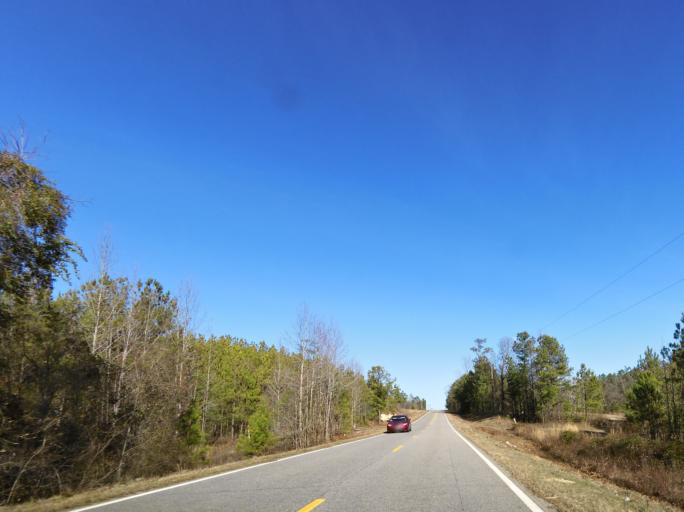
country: US
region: Georgia
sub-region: Crawford County
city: Knoxville
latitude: 32.7406
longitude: -83.9119
